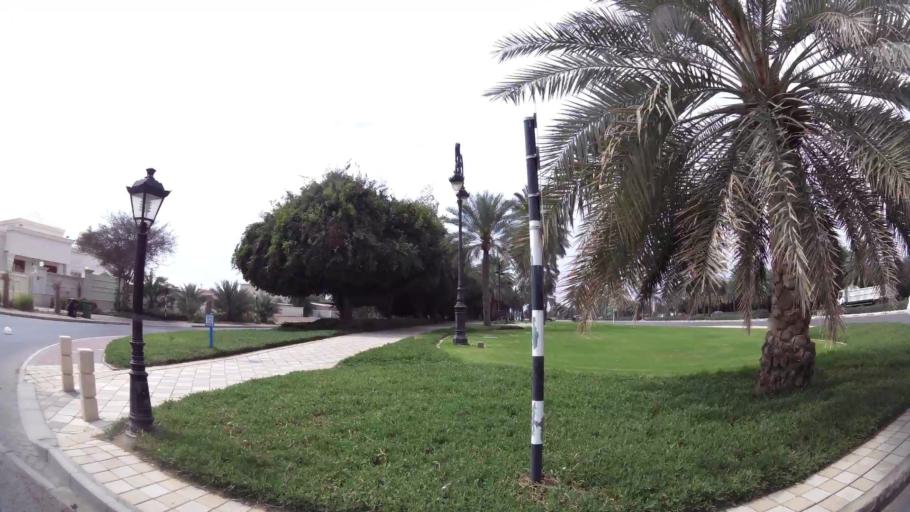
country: AE
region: Abu Dhabi
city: Al Ain
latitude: 24.2055
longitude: 55.7915
